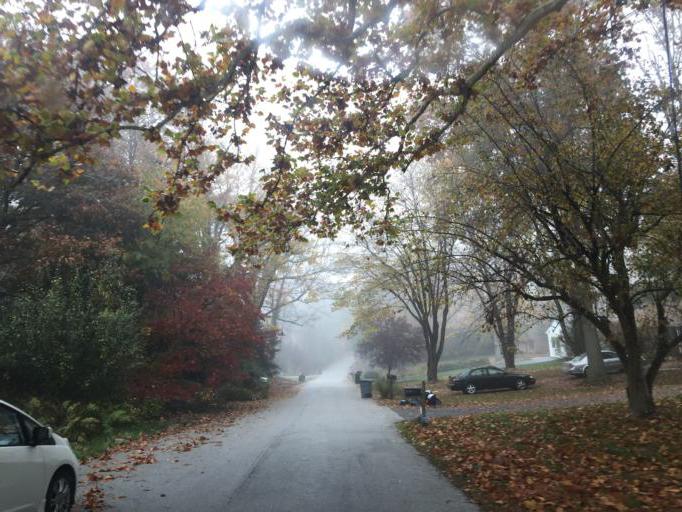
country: US
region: Maryland
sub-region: Howard County
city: Riverside
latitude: 39.1905
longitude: -76.8585
